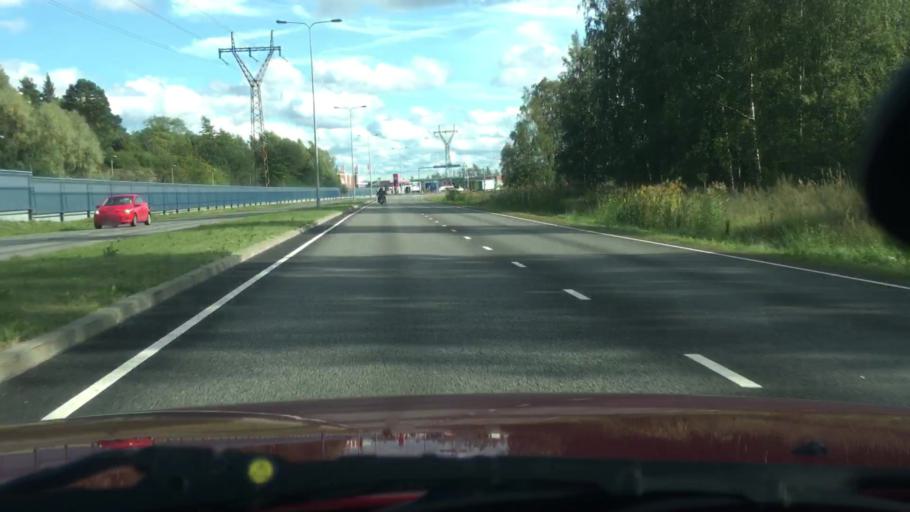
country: FI
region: Varsinais-Suomi
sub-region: Turku
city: Raisio
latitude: 60.4521
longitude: 22.1980
